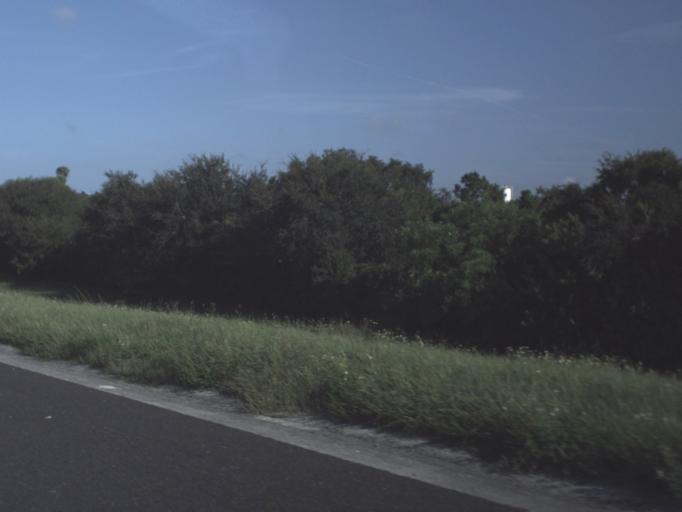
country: US
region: Florida
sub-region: Manatee County
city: West Samoset
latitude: 27.4788
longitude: -82.5527
